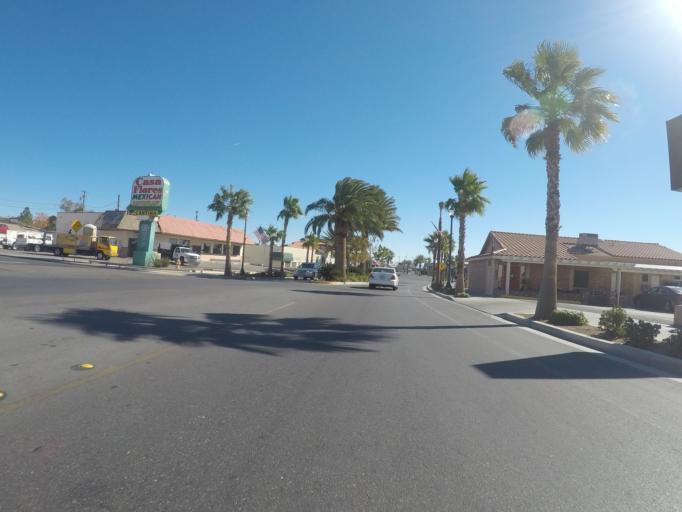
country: US
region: Nevada
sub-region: Clark County
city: Boulder City
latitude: 35.9745
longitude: -114.8440
